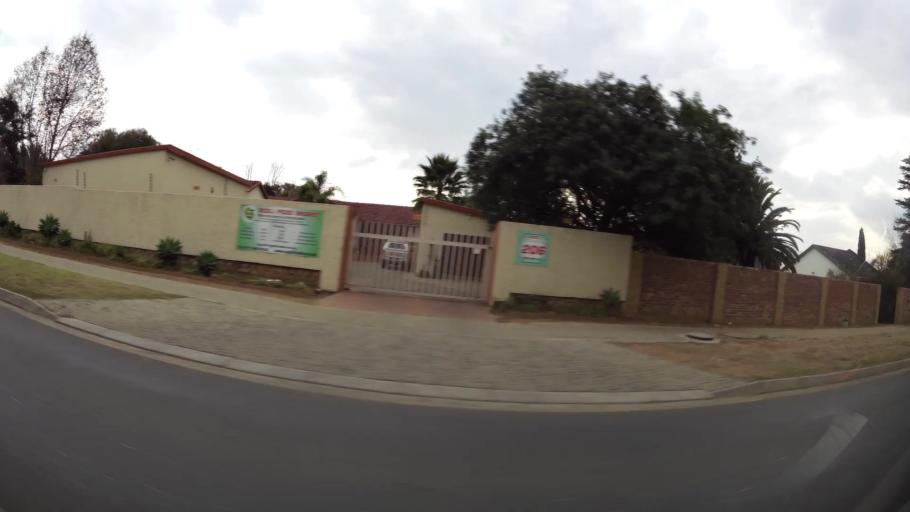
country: ZA
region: Gauteng
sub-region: Ekurhuleni Metropolitan Municipality
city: Benoni
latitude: -26.1420
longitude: 28.3460
